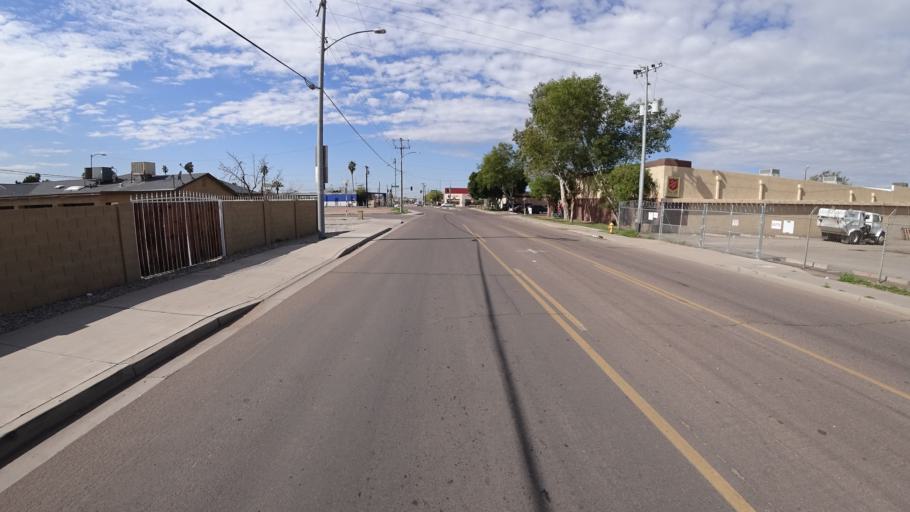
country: US
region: Arizona
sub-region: Maricopa County
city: Phoenix
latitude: 33.4314
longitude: -112.0723
